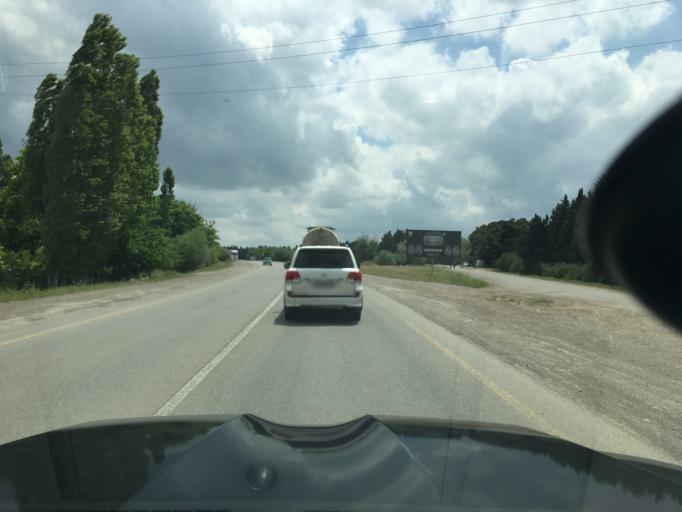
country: AZ
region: Tovuz
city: Qaraxanli
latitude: 41.0310
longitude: 45.5957
